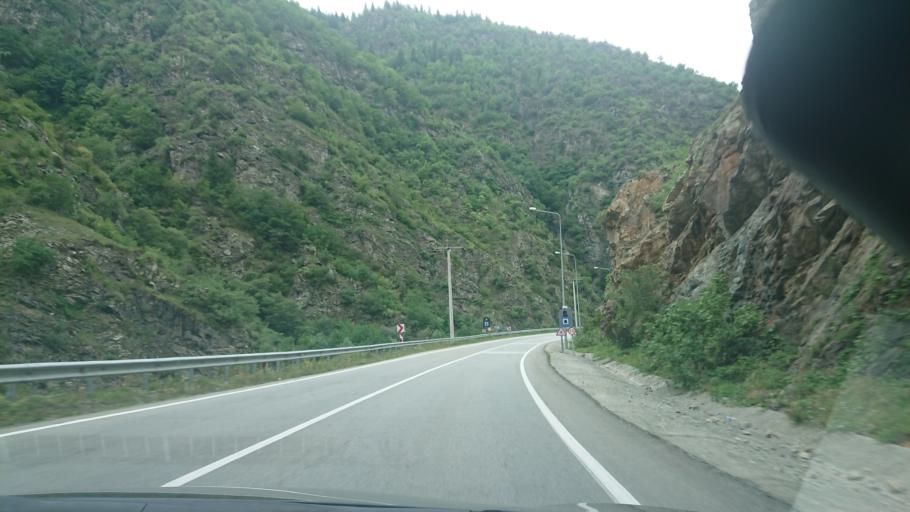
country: TR
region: Gumushane
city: Kurtun
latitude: 40.7344
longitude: 39.0049
